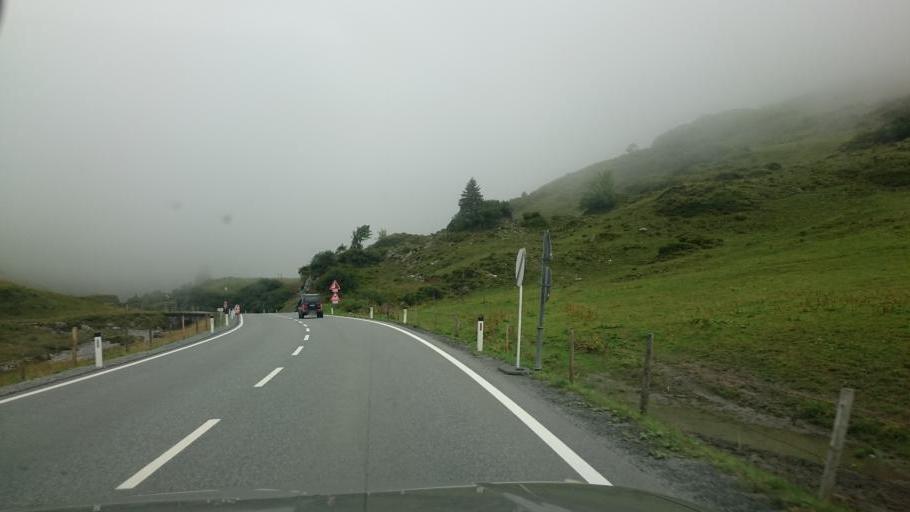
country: AT
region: Vorarlberg
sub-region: Politischer Bezirk Bludenz
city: Lech
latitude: 47.1539
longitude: 10.1649
